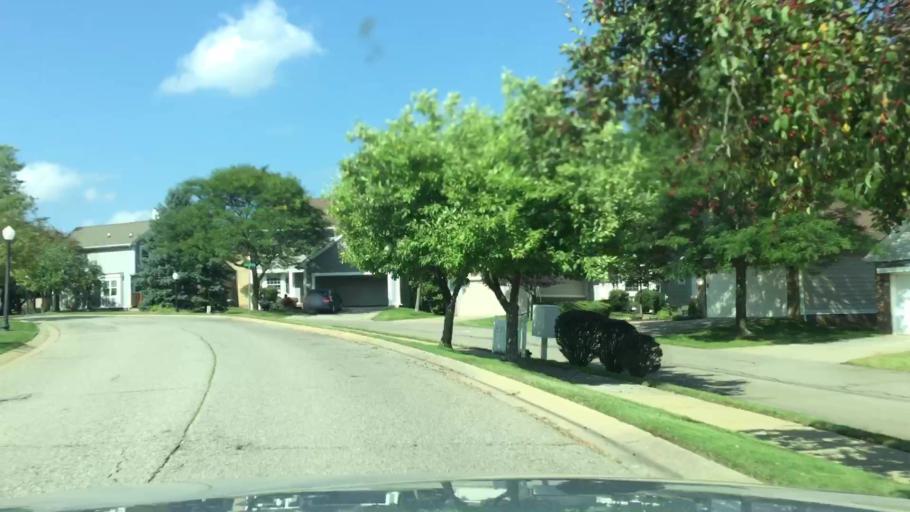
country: US
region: Michigan
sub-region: Oakland County
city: Walled Lake
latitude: 42.5239
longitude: -83.4564
